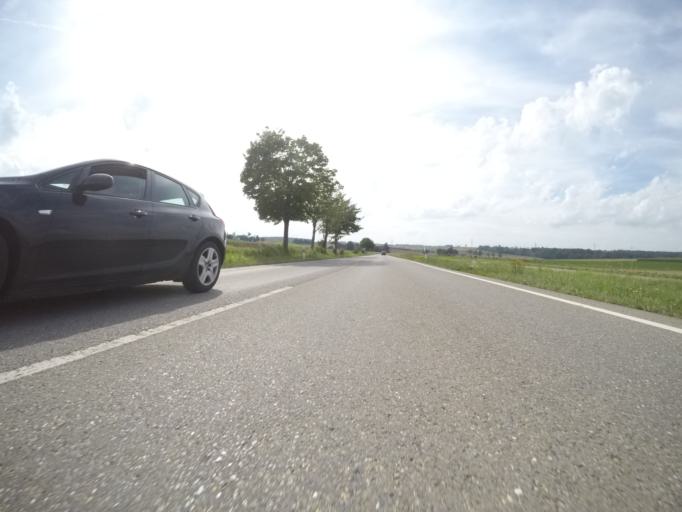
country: DE
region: Baden-Wuerttemberg
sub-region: Regierungsbezirk Stuttgart
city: Hemmingen
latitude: 48.8399
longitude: 9.0174
